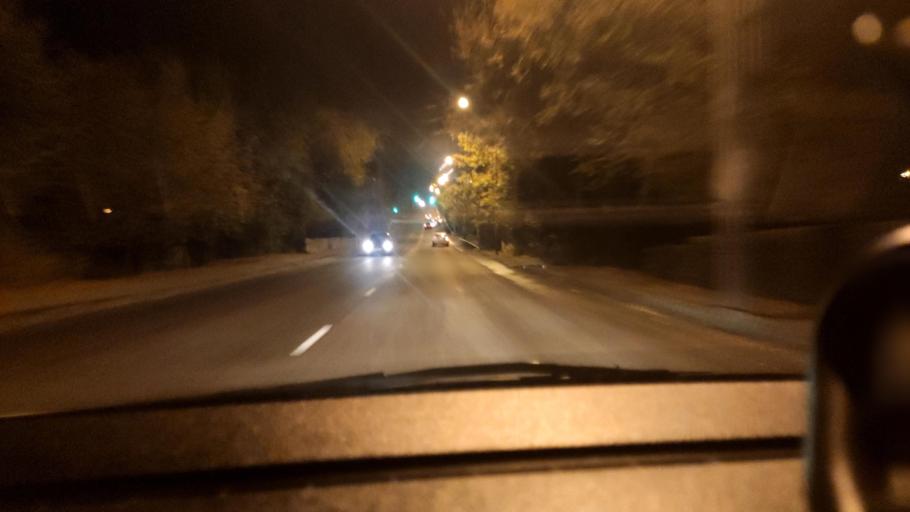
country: RU
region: Voronezj
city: Voronezh
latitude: 51.6925
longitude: 39.1647
